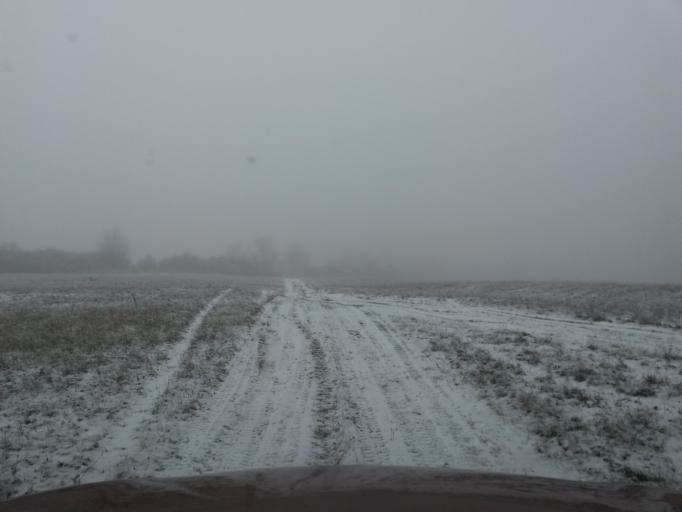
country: SK
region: Kosicky
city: Krompachy
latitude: 48.9814
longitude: 20.9884
